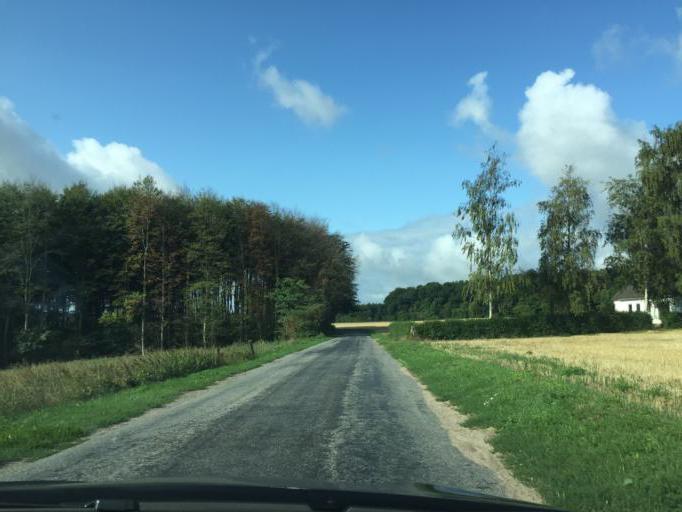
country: DK
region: South Denmark
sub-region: Faaborg-Midtfyn Kommune
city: Faaborg
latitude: 55.2003
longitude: 10.2845
